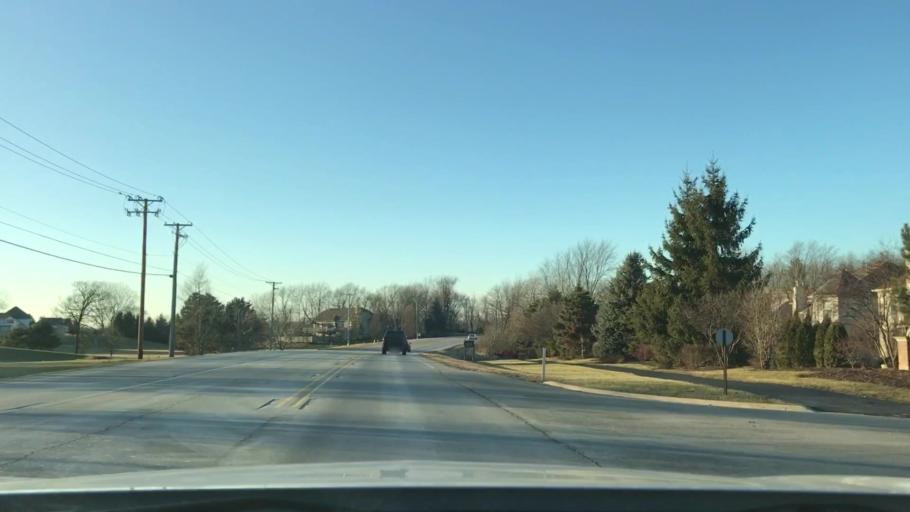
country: US
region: Illinois
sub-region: Kane County
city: Gilberts
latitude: 42.0786
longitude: -88.3780
